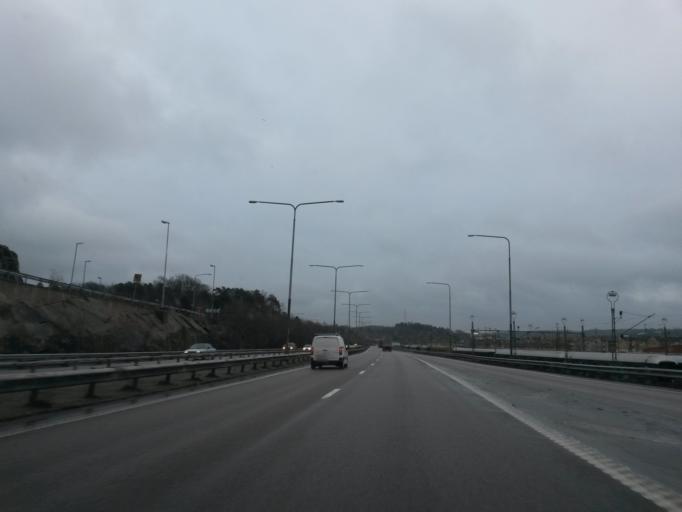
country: SE
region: Vaestra Goetaland
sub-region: Uddevalla Kommun
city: Uddevalla
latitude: 58.3557
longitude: 11.9154
